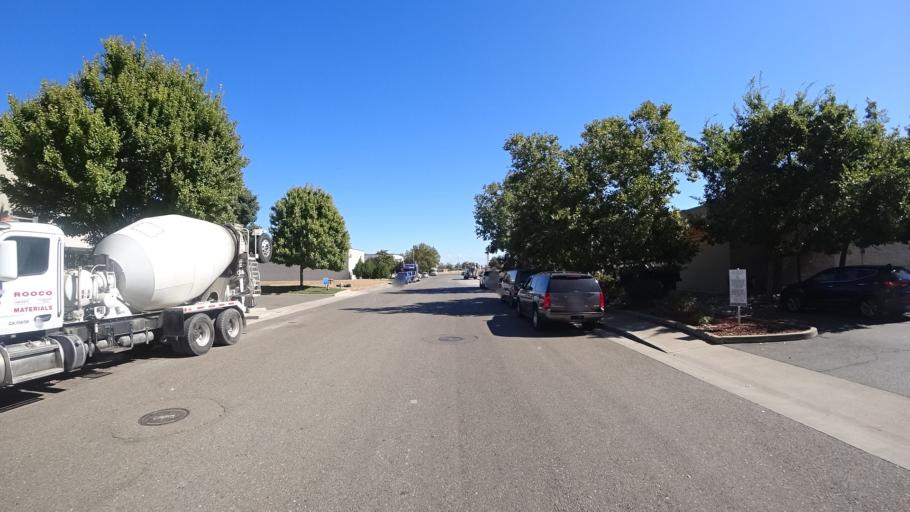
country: US
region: California
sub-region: Sacramento County
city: Elk Grove
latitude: 38.3755
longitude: -121.3585
